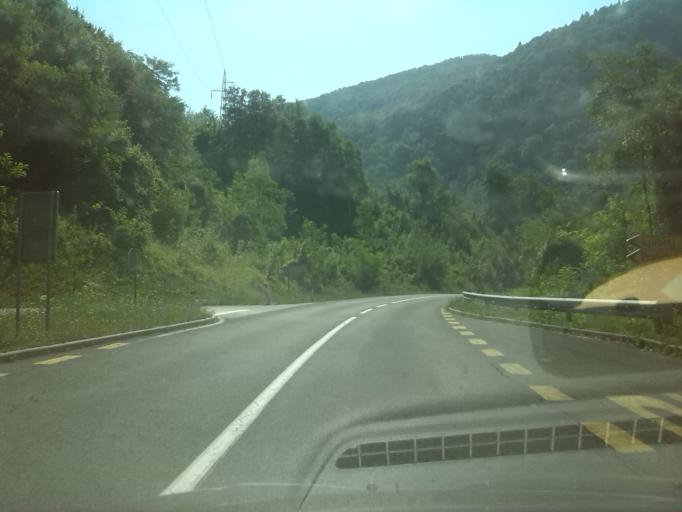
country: SI
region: Tolmin
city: Tolmin
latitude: 46.1705
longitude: 13.7535
